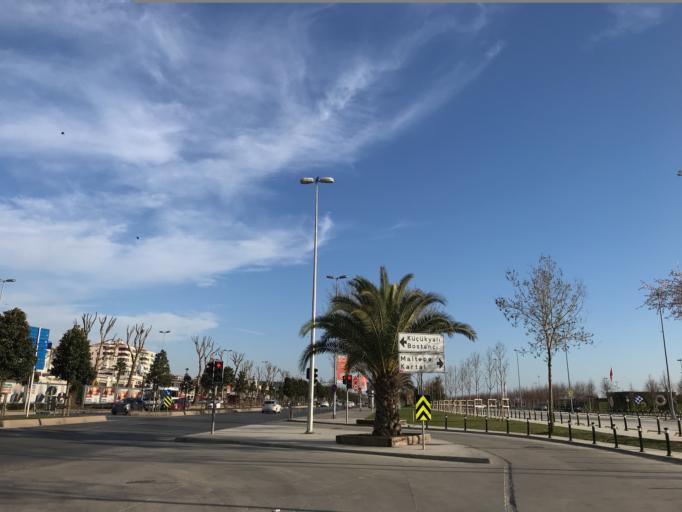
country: TR
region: Istanbul
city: Maltepe
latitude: 40.9292
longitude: 29.1203
